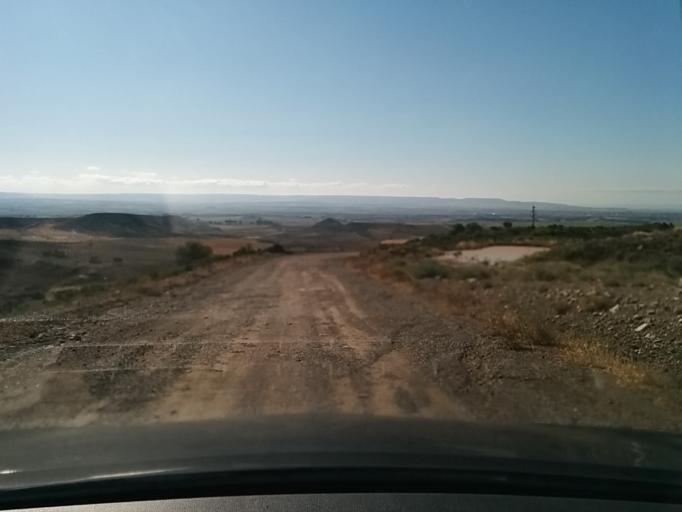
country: ES
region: Aragon
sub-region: Provincia de Zaragoza
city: Tauste
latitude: 42.0231
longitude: -1.3105
